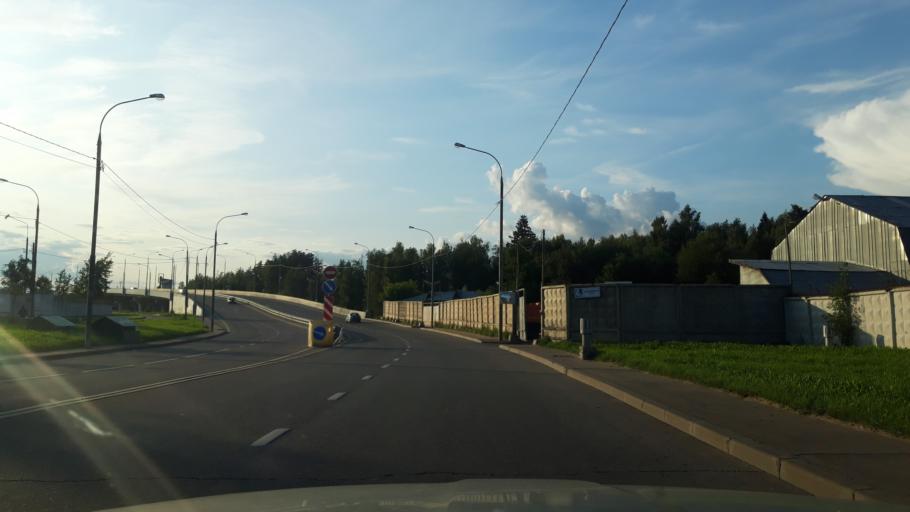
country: RU
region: Moscow
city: Zelenograd
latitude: 55.9926
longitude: 37.1655
